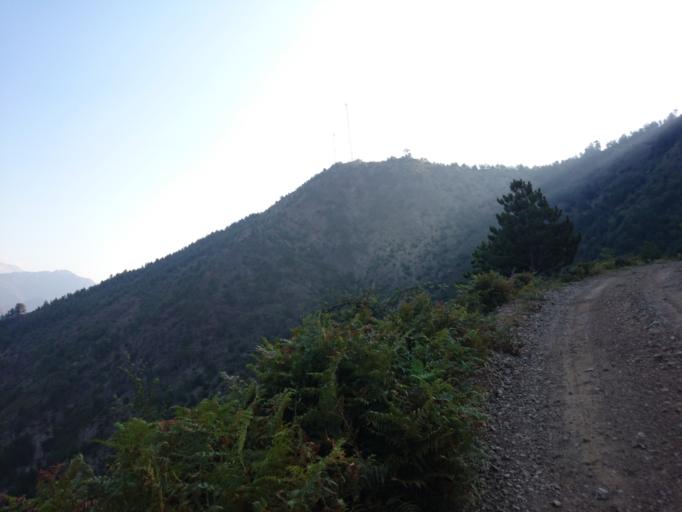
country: AL
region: Lezhe
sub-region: Rrethi i Mirdites
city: Orosh
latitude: 41.8670
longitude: 20.0893
